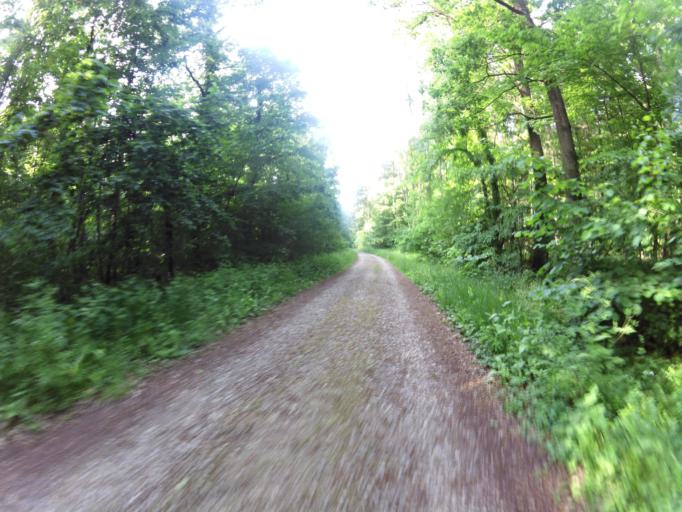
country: DE
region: Bavaria
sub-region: Regierungsbezirk Unterfranken
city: Ochsenfurt
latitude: 49.6812
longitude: 10.0655
